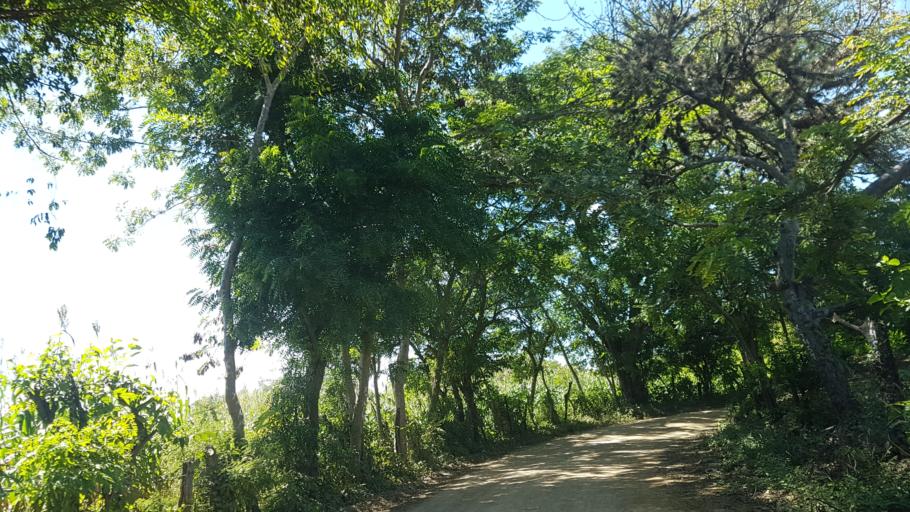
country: HN
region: El Paraiso
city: Santa Cruz
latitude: 13.7313
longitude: -86.6820
